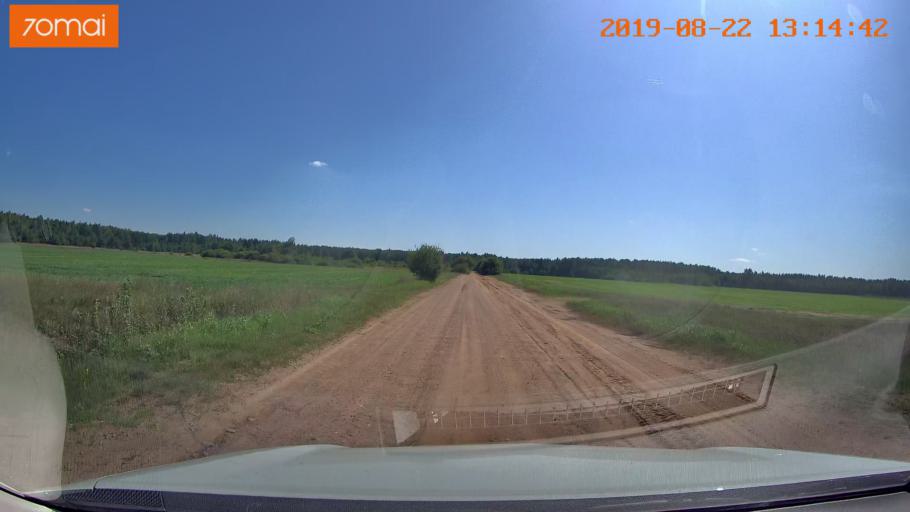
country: BY
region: Minsk
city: Prawdzinski
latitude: 53.2654
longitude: 27.8902
